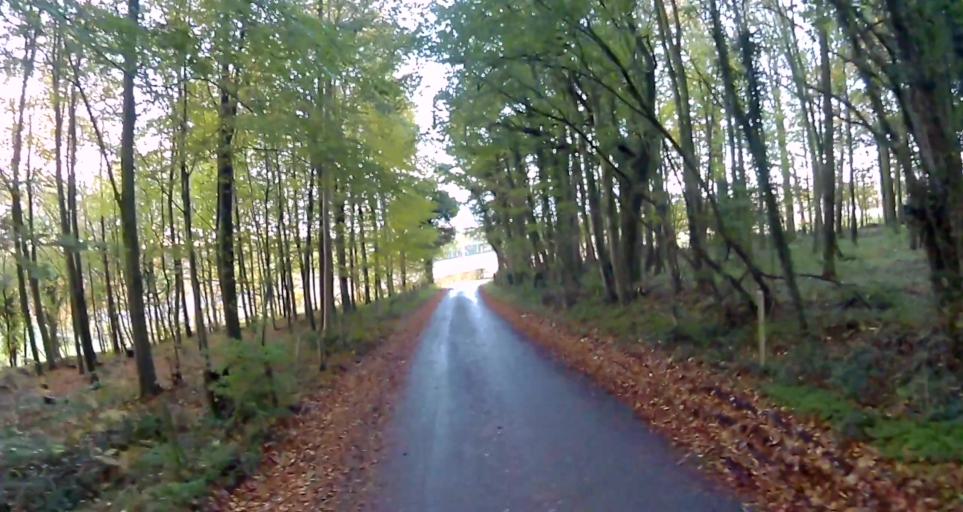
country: GB
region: England
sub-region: Hampshire
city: Basingstoke
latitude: 51.2156
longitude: -1.1011
